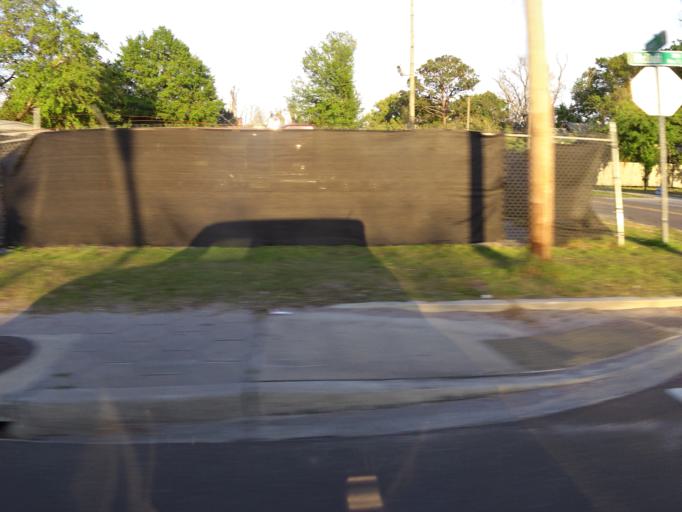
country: US
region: Florida
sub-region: Duval County
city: Jacksonville
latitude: 30.3244
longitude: -81.7054
